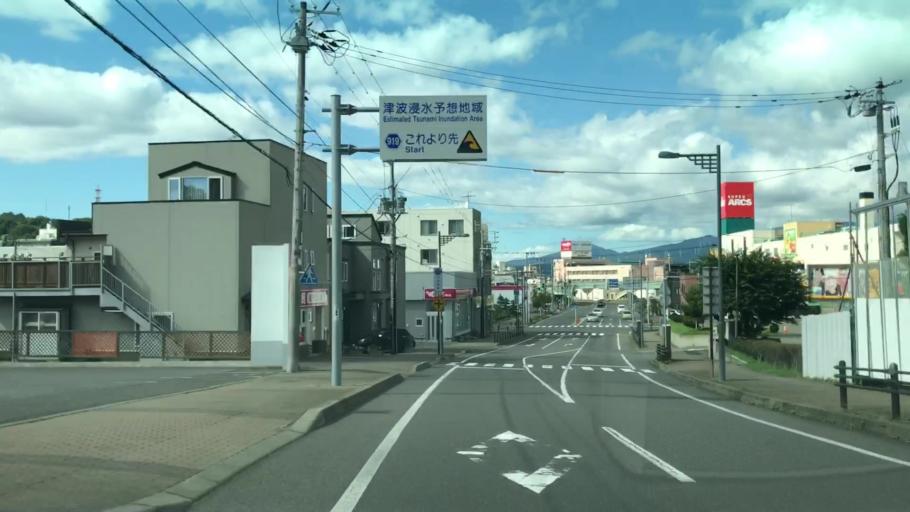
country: JP
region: Hokkaido
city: Muroran
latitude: 42.3136
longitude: 140.9754
